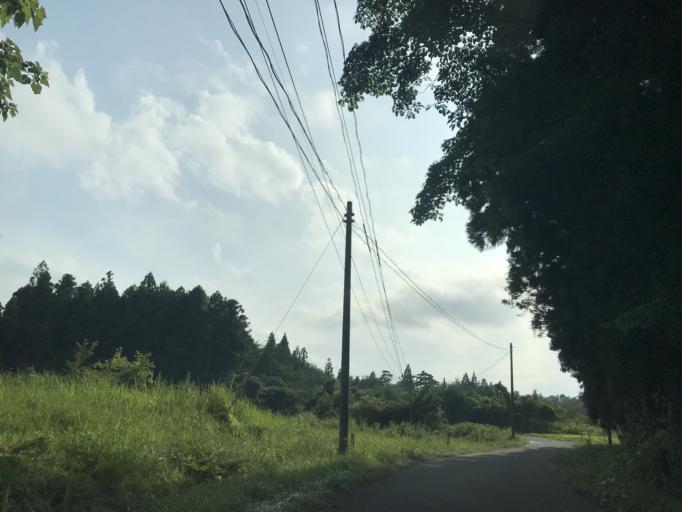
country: JP
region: Iwate
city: Ichinoseki
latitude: 38.8611
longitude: 141.1199
